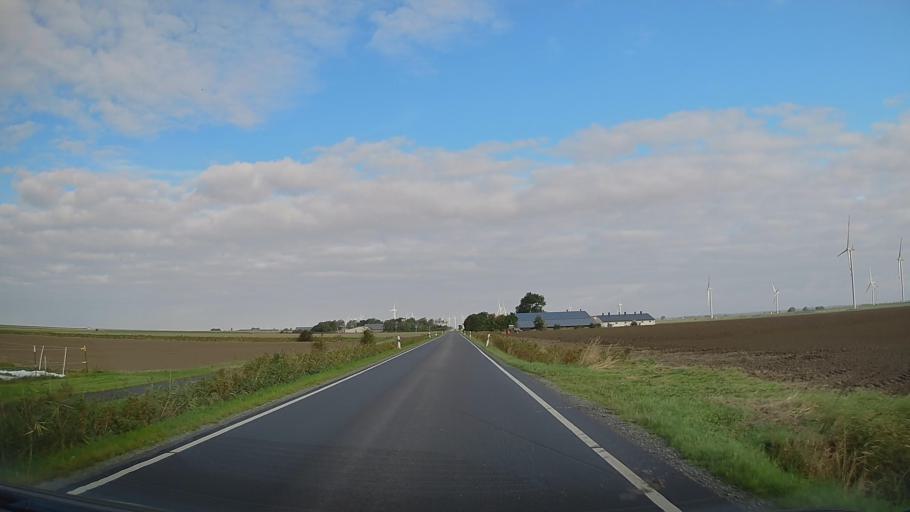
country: DE
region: Schleswig-Holstein
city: Reussenkoge
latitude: 54.5739
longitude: 8.9280
